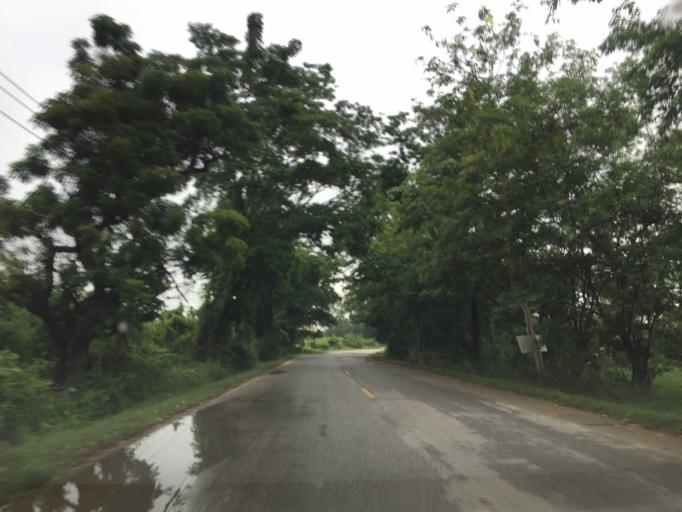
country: TH
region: Lamphun
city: Ban Thi
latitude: 18.6693
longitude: 99.0920
